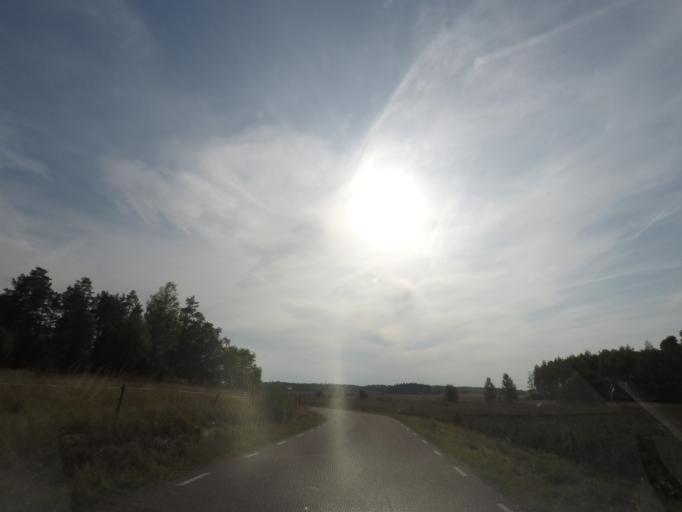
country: SE
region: Vaestmanland
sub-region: Kungsors Kommun
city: Kungsoer
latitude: 59.4977
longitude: 16.1533
